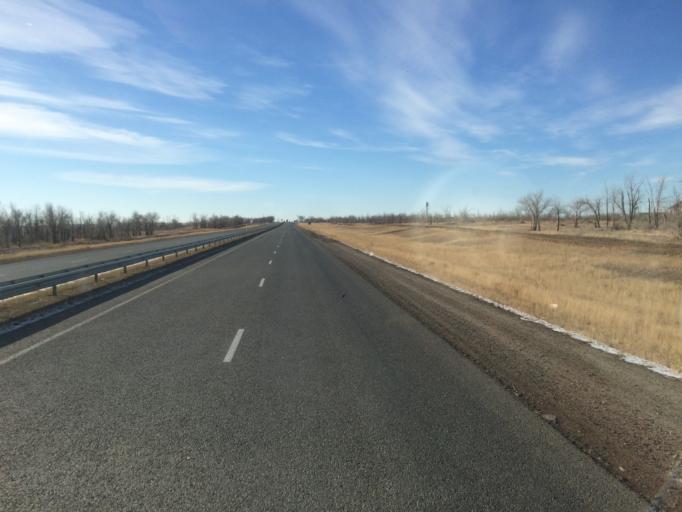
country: KZ
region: Aqtoebe
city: Aqtobe
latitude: 50.2669
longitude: 56.9664
